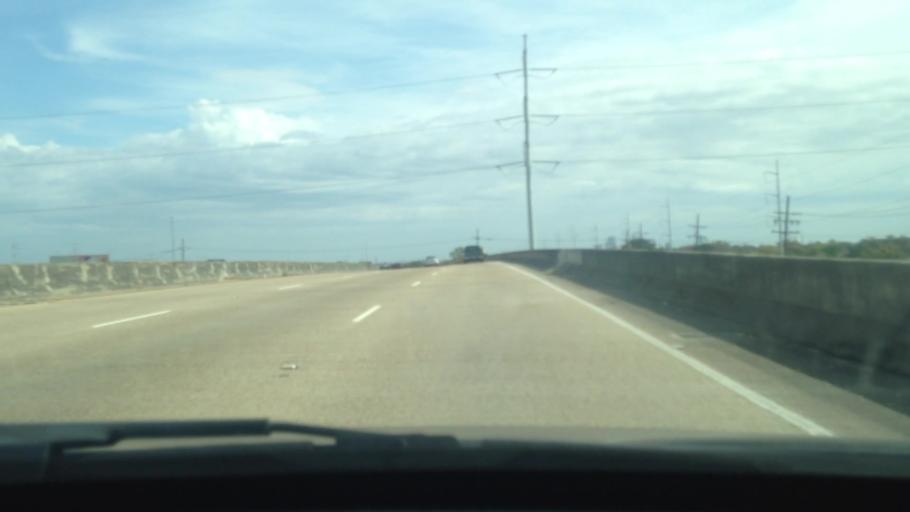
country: US
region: Louisiana
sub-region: Jefferson Parish
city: Metairie Terrace
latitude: 29.9709
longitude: -90.1632
